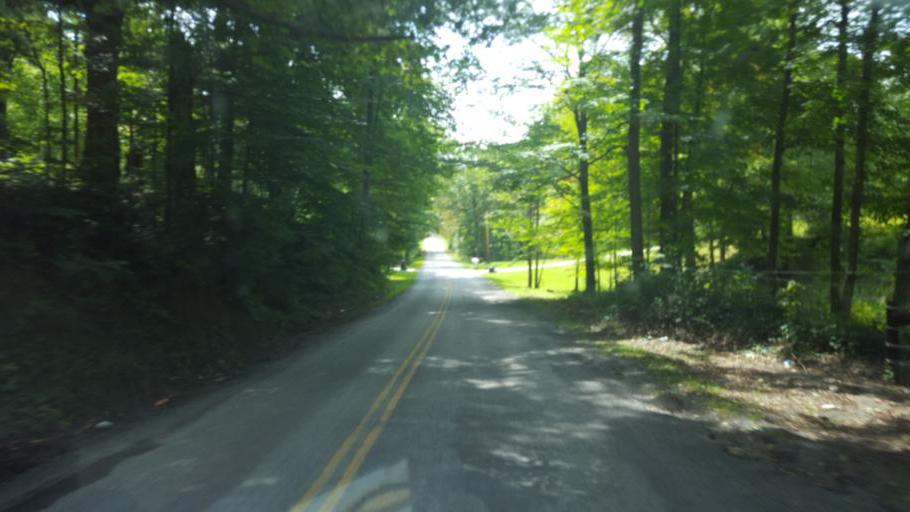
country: US
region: Ohio
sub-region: Geauga County
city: Middlefield
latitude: 41.4320
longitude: -80.9732
